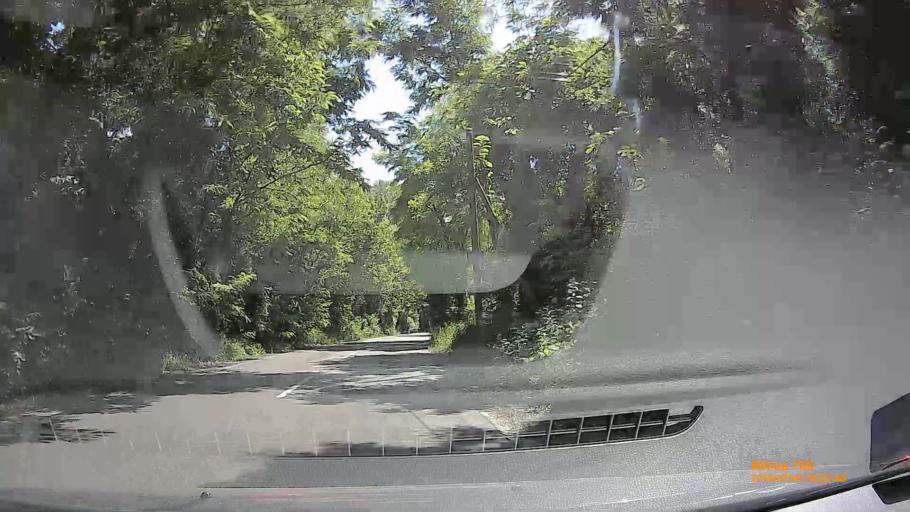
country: HU
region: Komarom-Esztergom
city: Tatabanya
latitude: 47.5514
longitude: 18.3797
